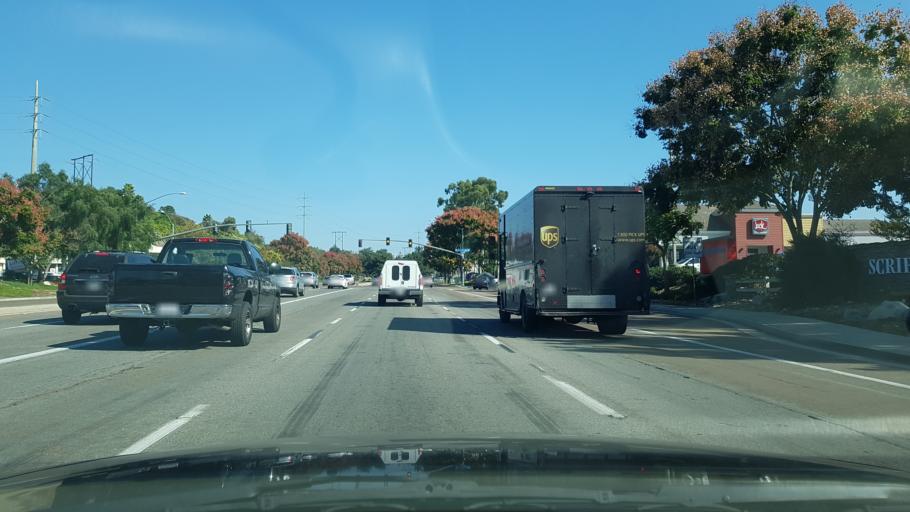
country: US
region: California
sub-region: San Diego County
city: Poway
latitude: 32.9374
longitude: -117.1019
